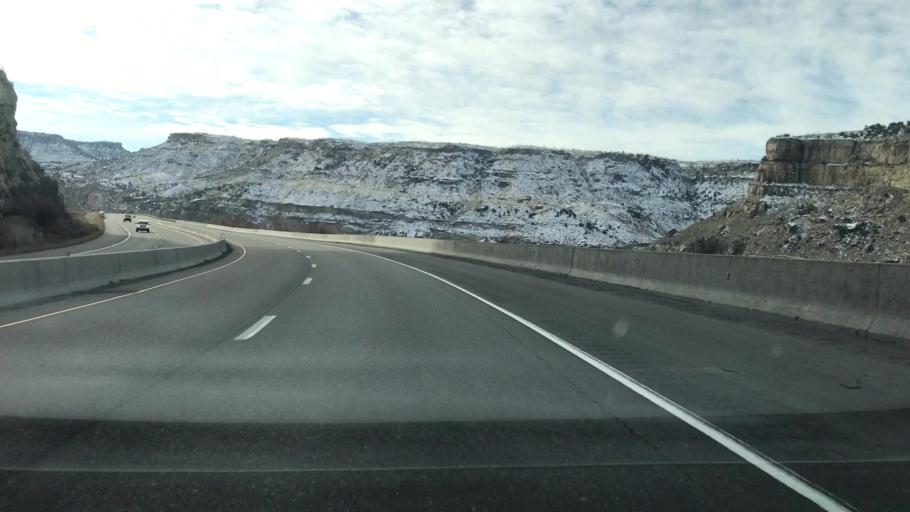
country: US
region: Colorado
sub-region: Mesa County
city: Palisade
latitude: 39.2602
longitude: -108.2592
